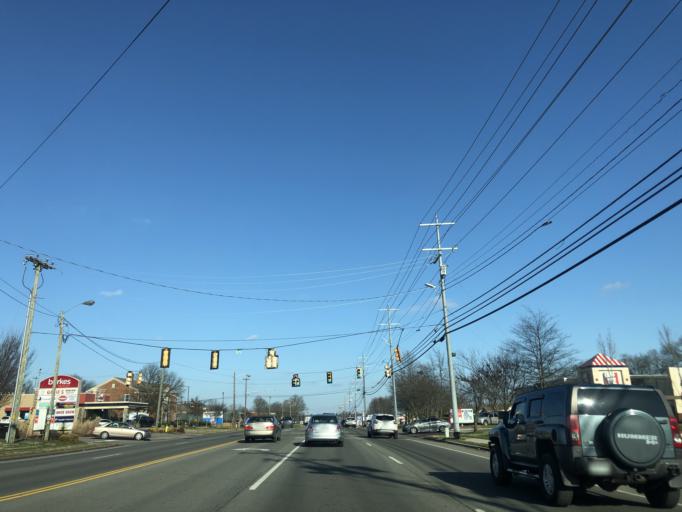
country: US
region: Tennessee
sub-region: Sumner County
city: Gallatin
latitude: 36.3809
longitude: -86.4632
